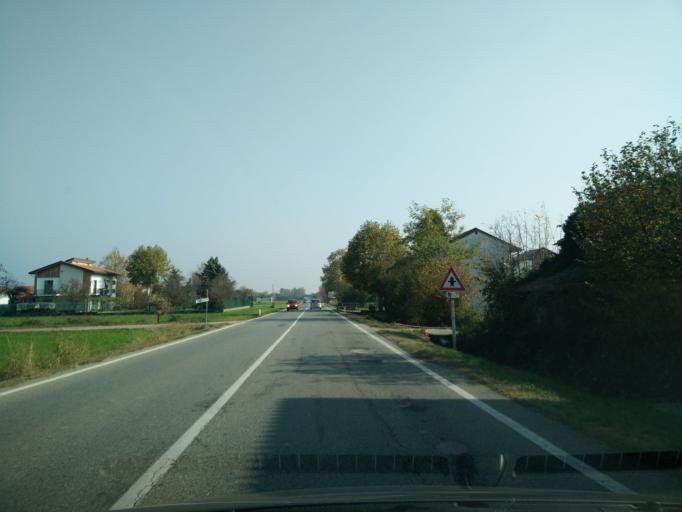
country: IT
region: Piedmont
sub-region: Provincia di Torino
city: Leini
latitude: 45.1816
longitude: 7.6787
